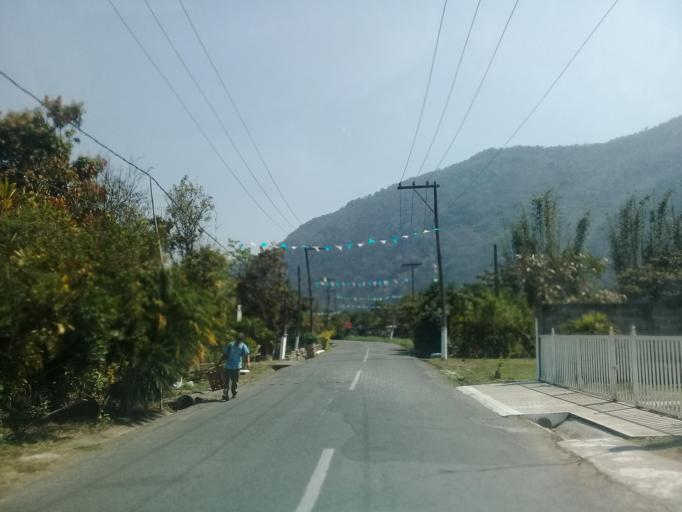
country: MX
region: Veracruz
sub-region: Ixtaczoquitlan
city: Capoluca
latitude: 18.8034
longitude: -96.9929
